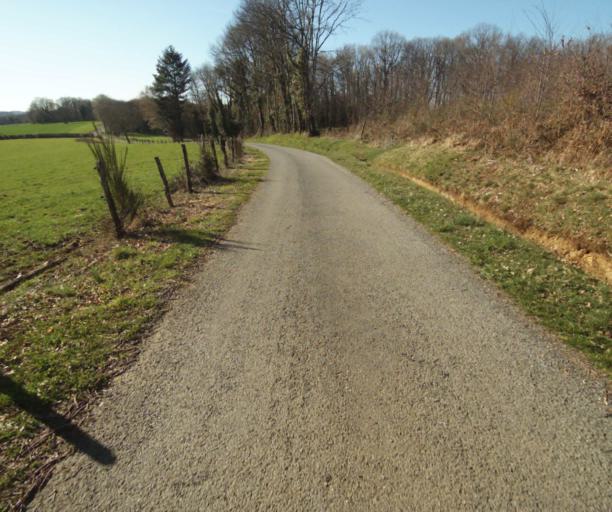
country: FR
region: Limousin
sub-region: Departement de la Correze
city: Chamboulive
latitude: 45.3963
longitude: 1.6796
